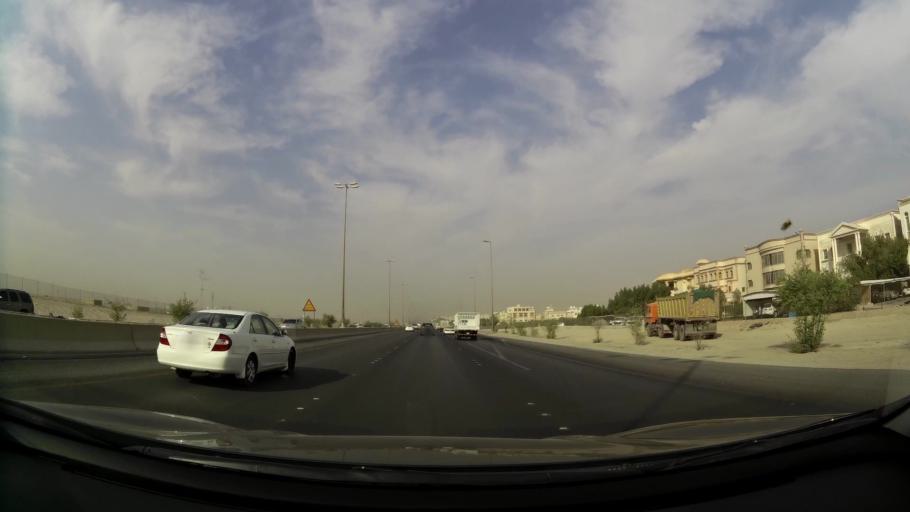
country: KW
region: Al Asimah
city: Ar Rabiyah
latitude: 29.2675
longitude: 47.8848
